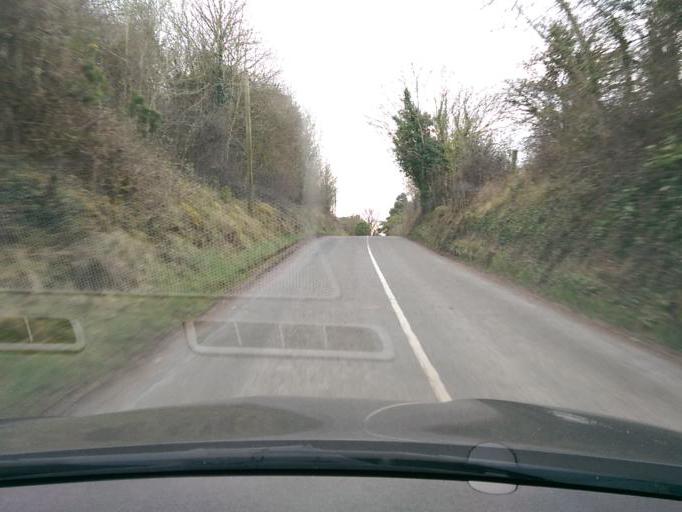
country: IE
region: Leinster
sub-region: An Iarmhi
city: Athlone
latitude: 53.3221
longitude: -7.9581
